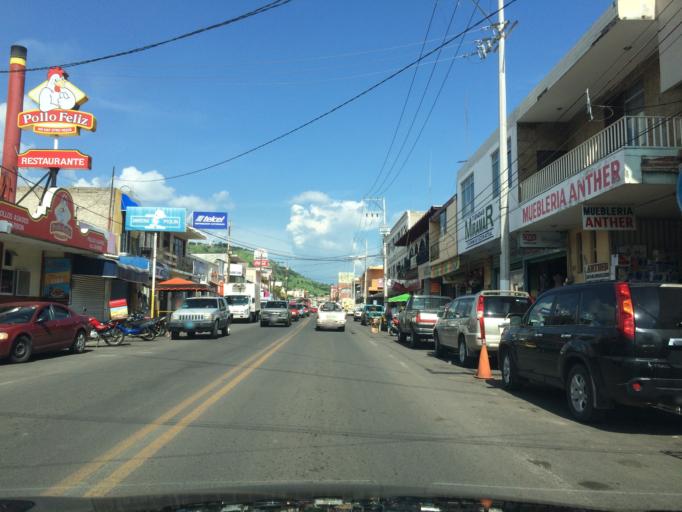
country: MX
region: Nayarit
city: Ixtlan del Rio
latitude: 21.0355
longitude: -104.3713
